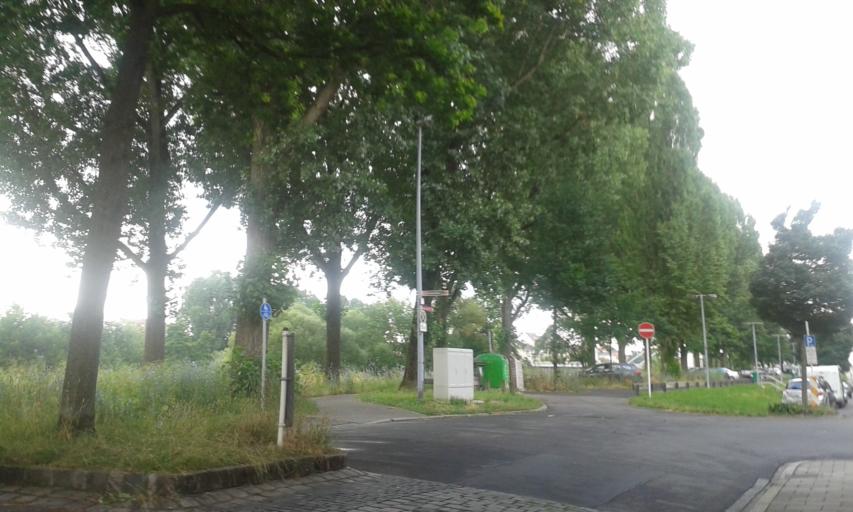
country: DE
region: Bavaria
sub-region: Upper Franconia
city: Bamberg
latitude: 49.8987
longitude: 10.8836
